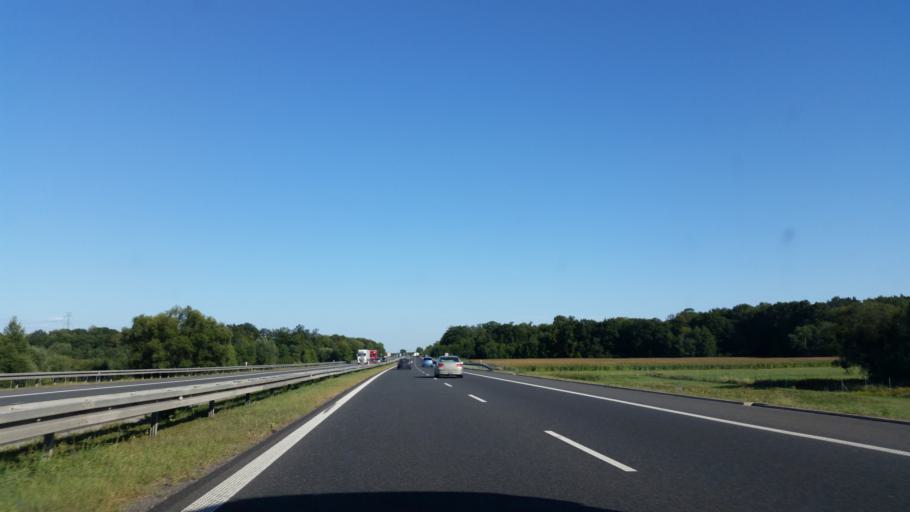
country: PL
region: Opole Voivodeship
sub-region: Powiat brzeski
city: Olszanka
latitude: 50.7322
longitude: 17.5024
